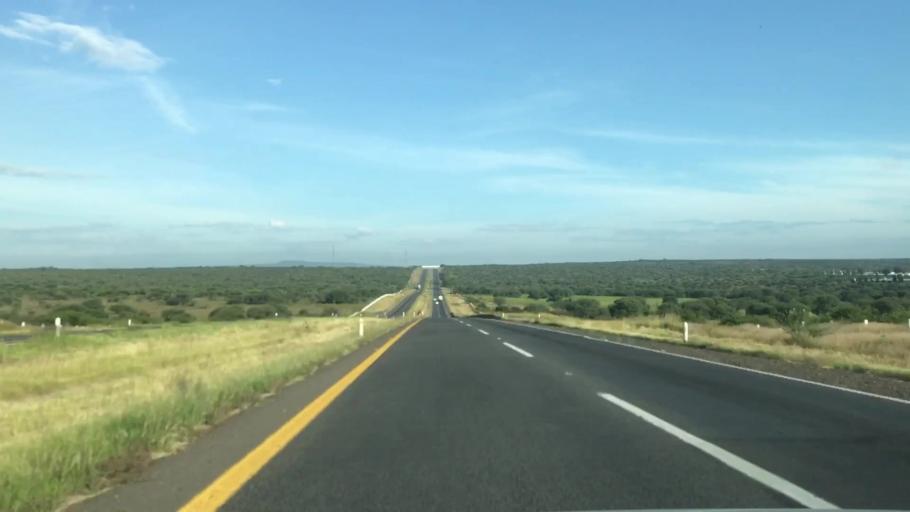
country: MX
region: Jalisco
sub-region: Union de San Antonio
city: San Jose del Caliche (El Caliche)
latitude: 21.1761
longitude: -101.8738
